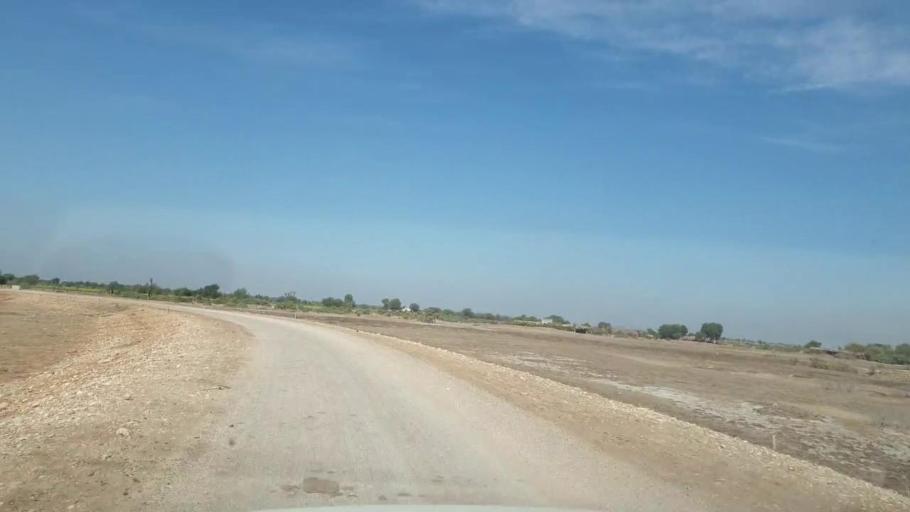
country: PK
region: Sindh
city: Mirpur Khas
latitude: 25.6492
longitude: 69.1913
